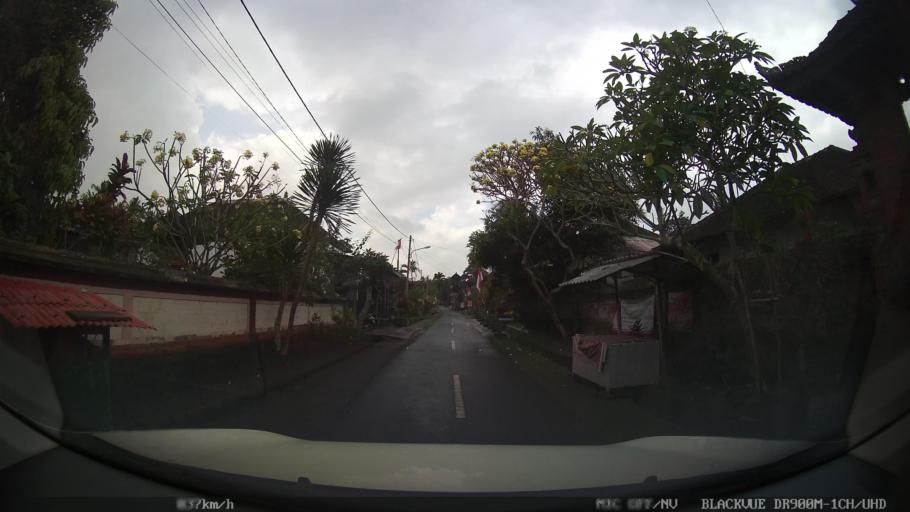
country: ID
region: Bali
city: Banjar Tebongkang
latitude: -8.5265
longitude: 115.2372
